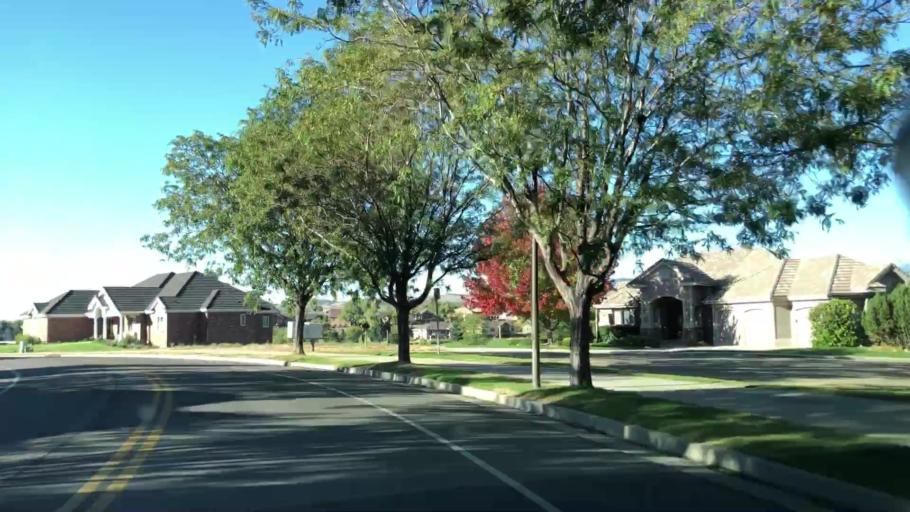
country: US
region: Colorado
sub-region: Larimer County
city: Loveland
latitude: 40.3994
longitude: -105.1490
